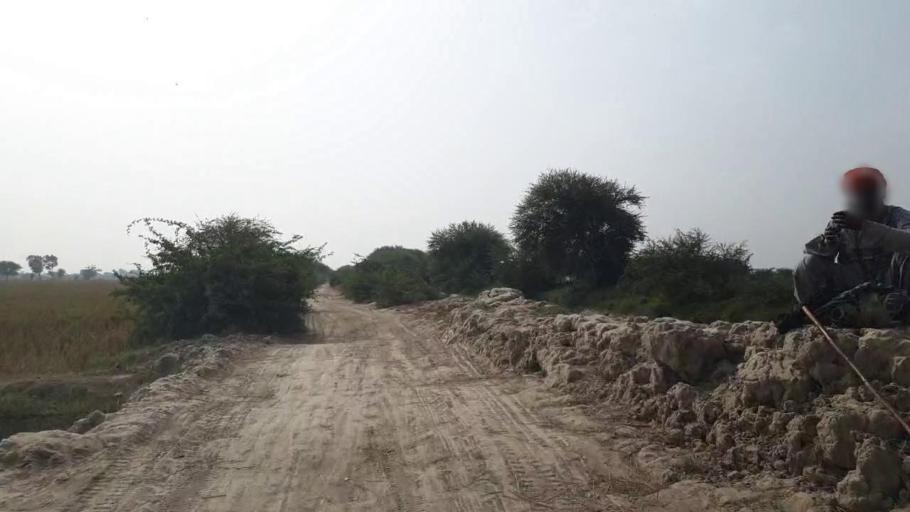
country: PK
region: Sindh
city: Kario
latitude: 24.7838
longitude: 68.5637
